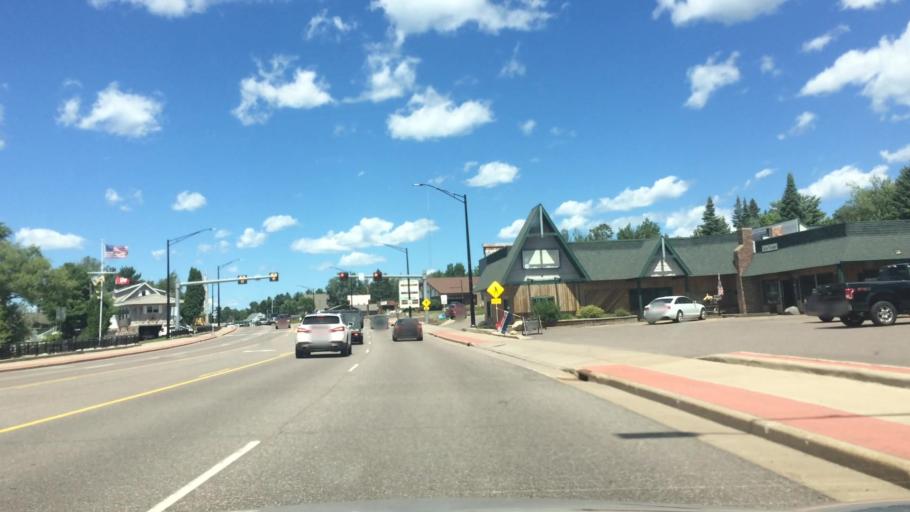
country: US
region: Wisconsin
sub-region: Vilas County
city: Lac du Flambeau
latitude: 45.8774
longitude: -89.7040
